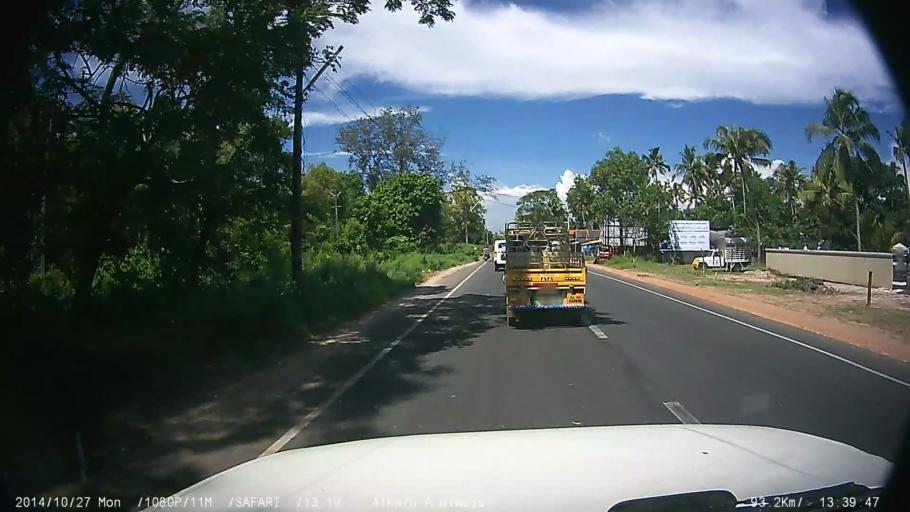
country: IN
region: Kerala
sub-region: Alappuzha
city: Shertallai
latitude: 9.6290
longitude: 76.3331
